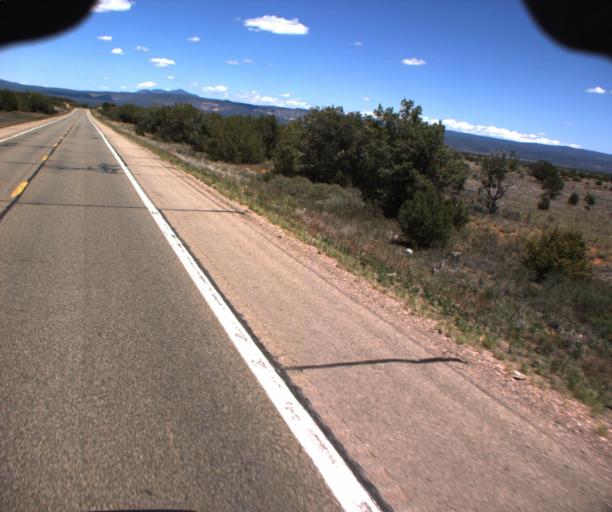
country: US
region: Arizona
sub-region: Yavapai County
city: Paulden
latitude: 34.9602
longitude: -112.4153
